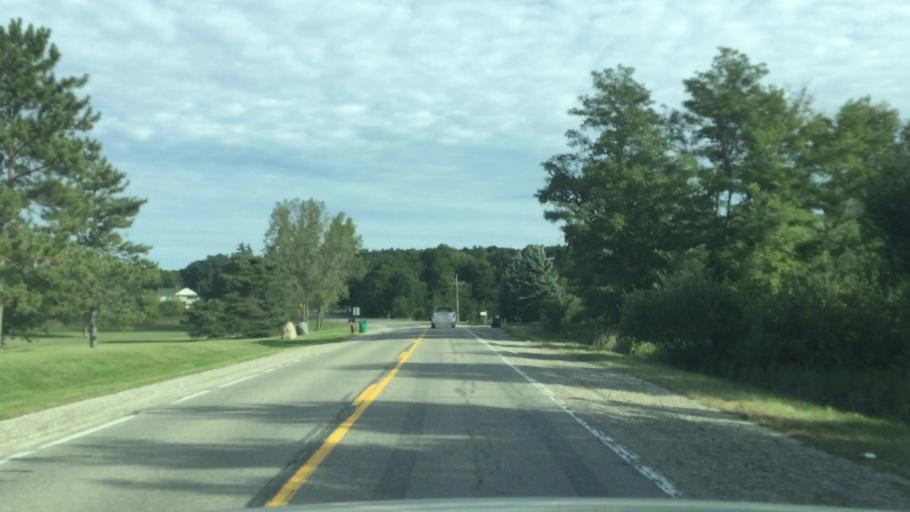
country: US
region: Michigan
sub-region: Livingston County
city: Howell
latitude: 42.5717
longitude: -83.8930
